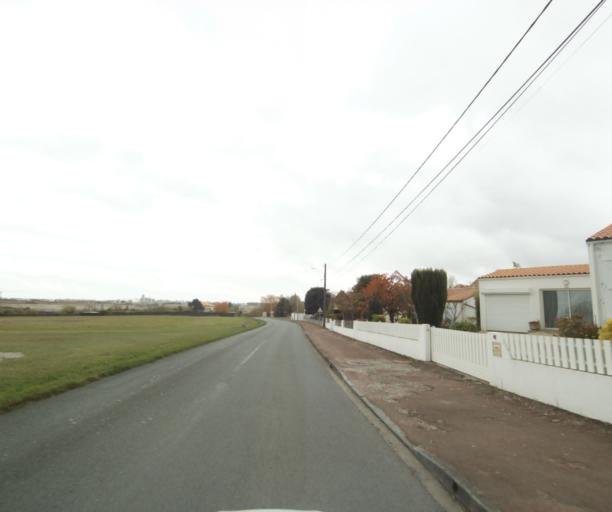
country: FR
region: Poitou-Charentes
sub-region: Departement de la Charente-Maritime
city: Saintes
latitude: 45.7303
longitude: -0.6496
